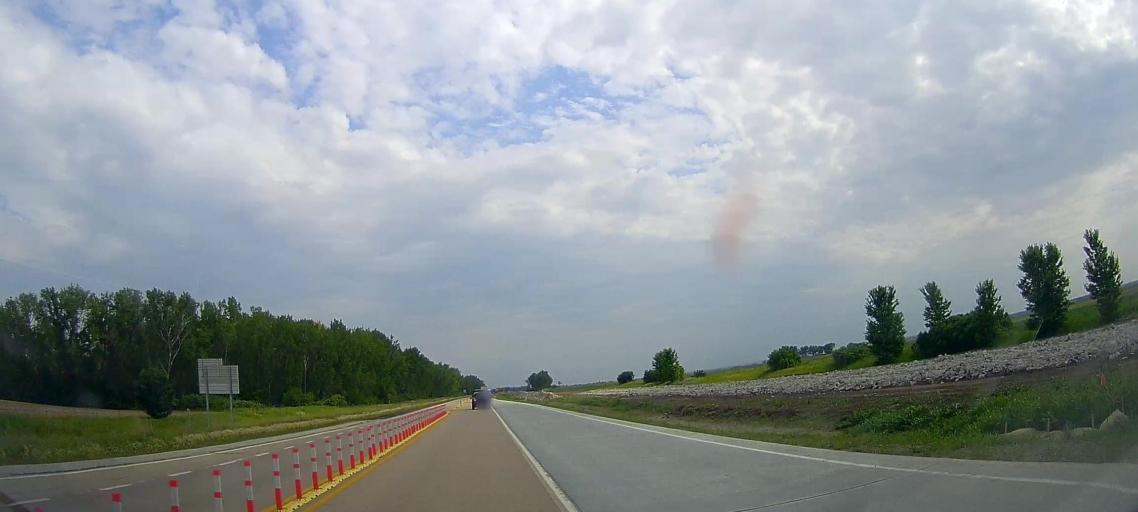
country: US
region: Nebraska
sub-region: Washington County
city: Blair
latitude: 41.7061
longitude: -96.0436
